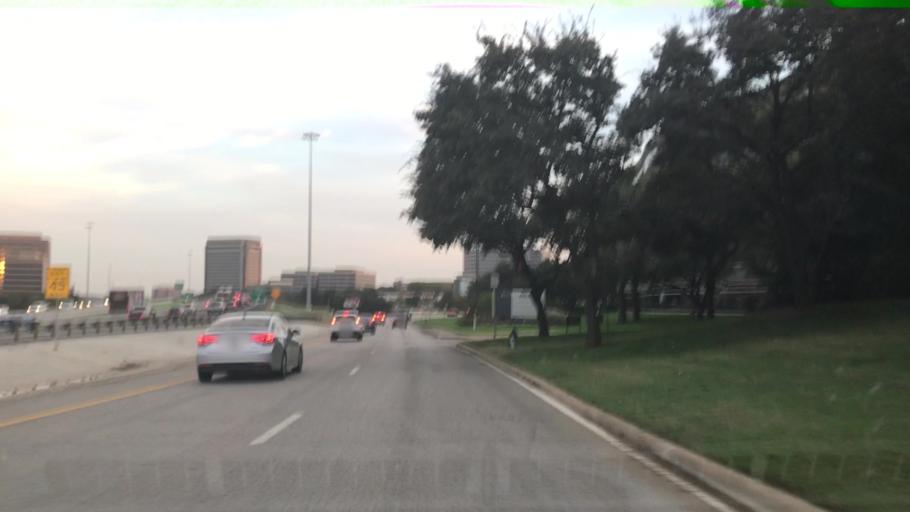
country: US
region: Texas
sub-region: Dallas County
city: Irving
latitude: 32.8710
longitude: -96.9460
